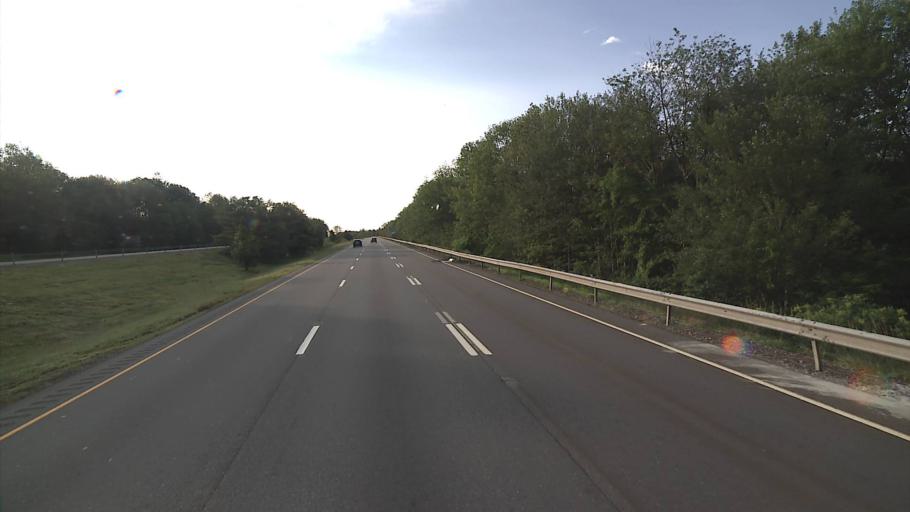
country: US
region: Connecticut
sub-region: New London County
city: Colchester
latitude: 41.5777
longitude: -72.3523
